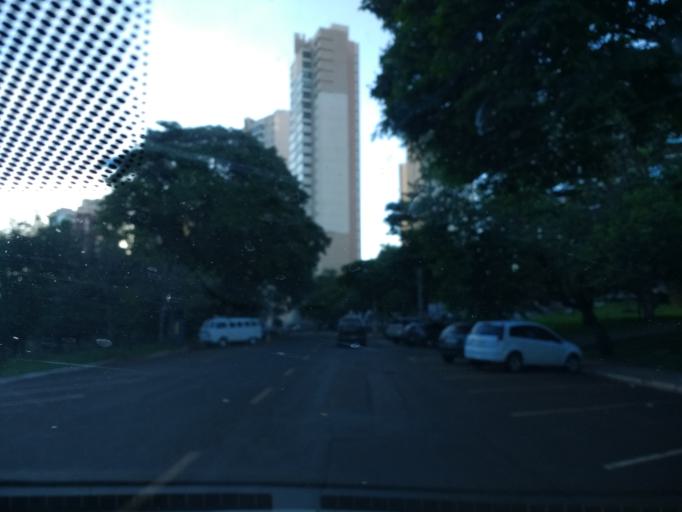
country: BR
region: Parana
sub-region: Londrina
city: Londrina
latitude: -23.3359
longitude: -51.1518
